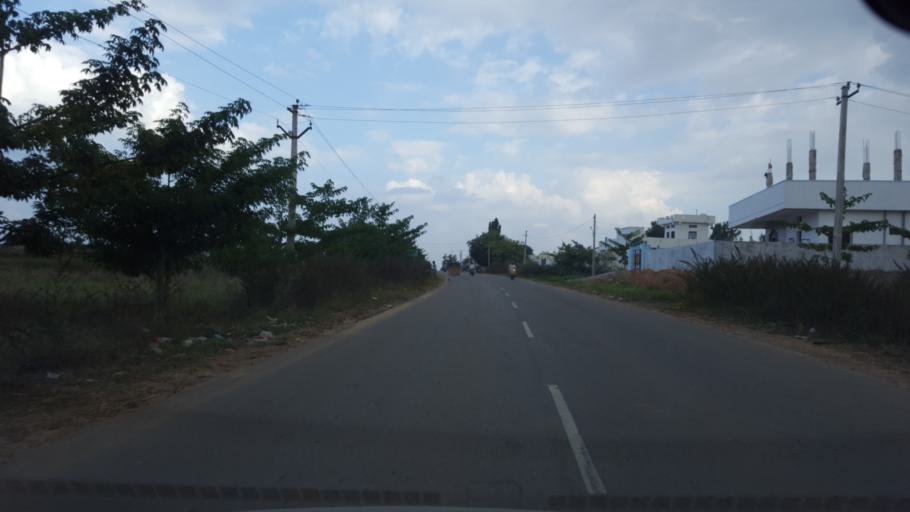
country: IN
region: Telangana
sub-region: Mahbubnagar
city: Mahbubnagar
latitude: 16.7604
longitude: 77.9557
